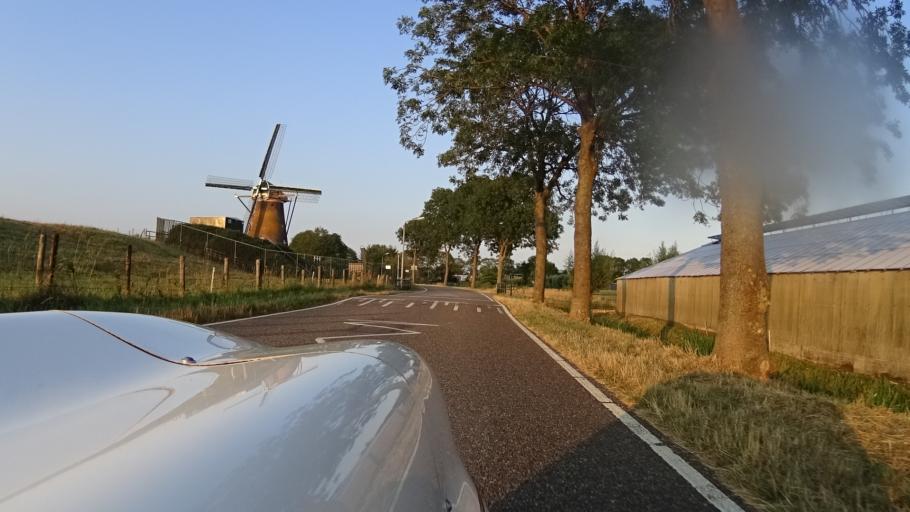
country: NL
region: South Holland
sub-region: Gemeente Kaag en Braassem
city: Oude Wetering
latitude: 52.2157
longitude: 4.6320
